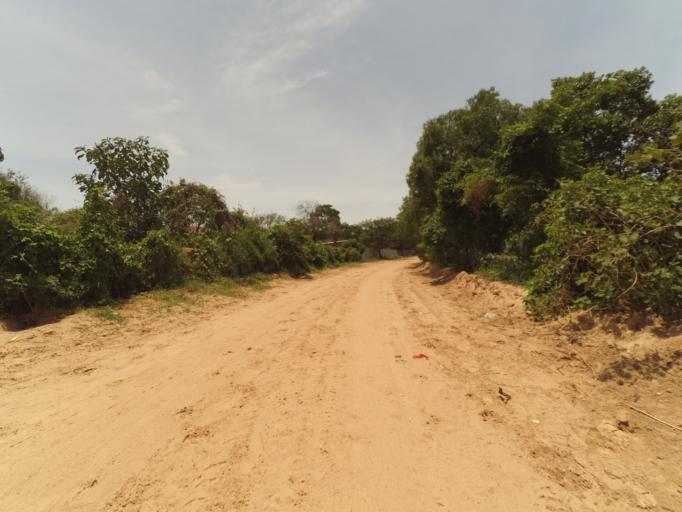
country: BO
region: Santa Cruz
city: Santa Cruz de la Sierra
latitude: -17.8179
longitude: -63.2564
